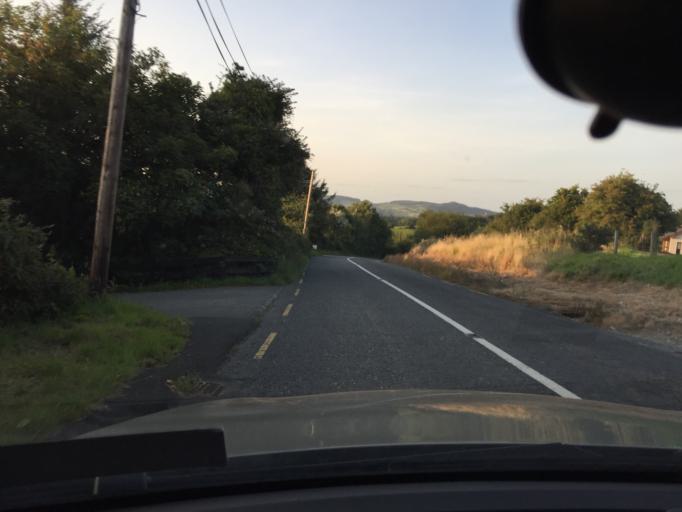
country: IE
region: Leinster
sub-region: Wicklow
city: Enniskerry
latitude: 53.1631
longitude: -6.1657
